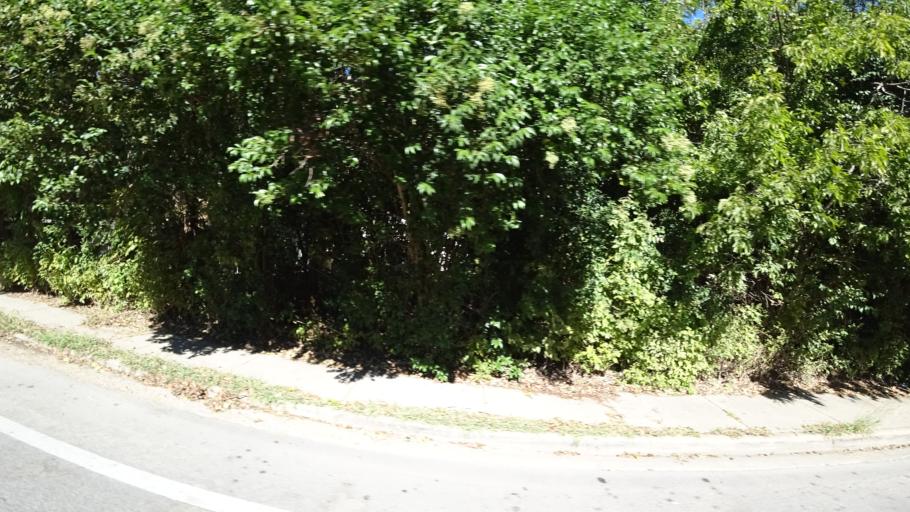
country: US
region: Texas
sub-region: Travis County
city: Rollingwood
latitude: 30.2239
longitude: -97.7831
